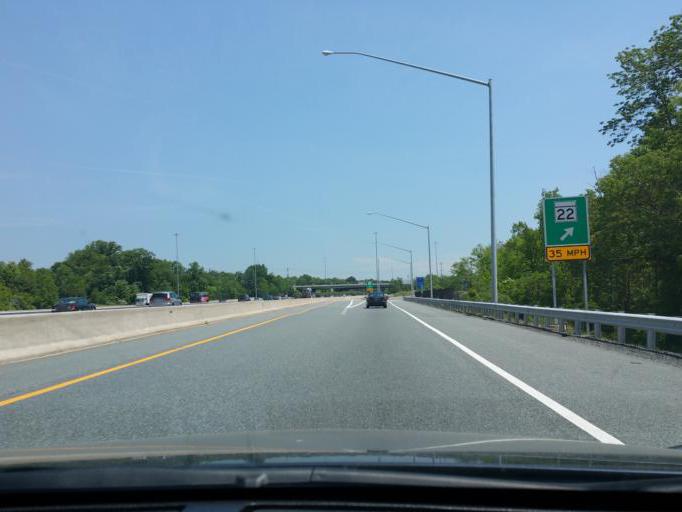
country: US
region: Maryland
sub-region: Harford County
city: Aberdeen
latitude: 39.5226
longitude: -76.1962
